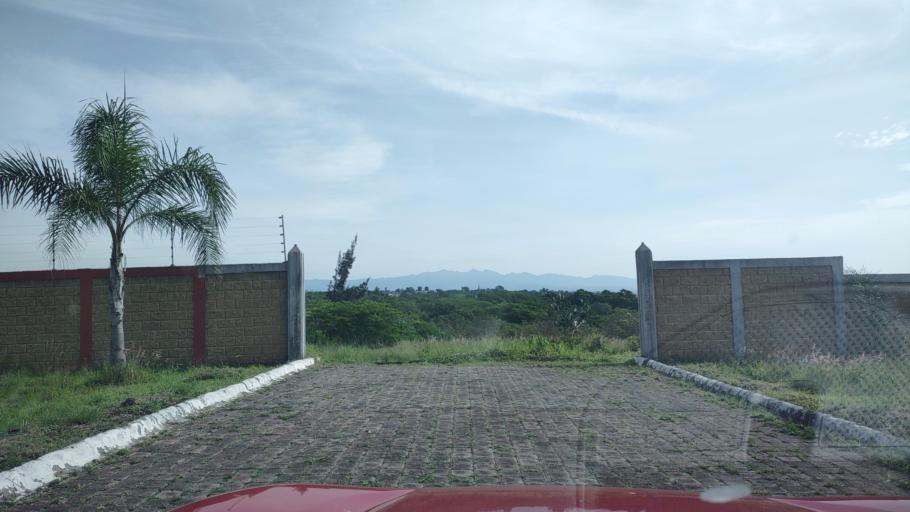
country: MX
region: Veracruz
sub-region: Emiliano Zapata
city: Dos Rios
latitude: 19.4736
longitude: -96.8249
